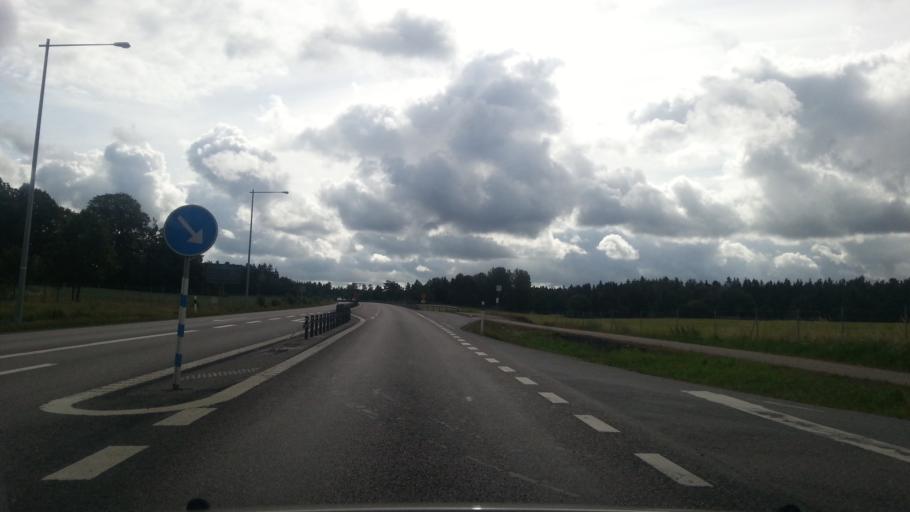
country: SE
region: Vaestra Goetaland
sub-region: Vanersborgs Kommun
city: Vargon
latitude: 58.2802
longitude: 12.4471
